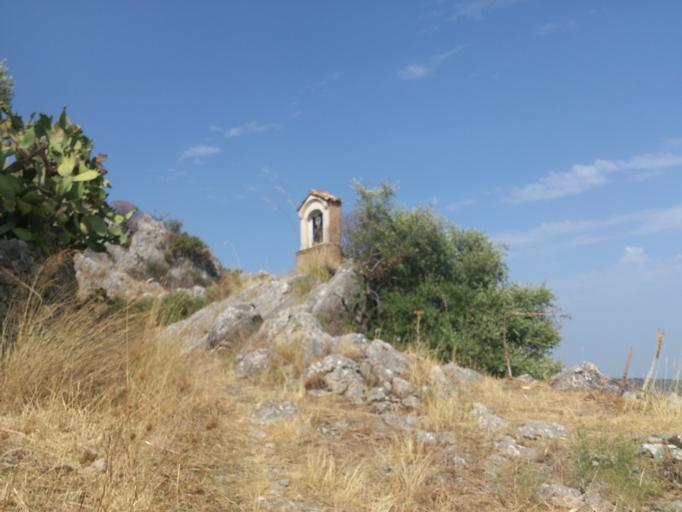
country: IT
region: Calabria
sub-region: Provincia di Reggio Calabria
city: Pazzano
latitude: 38.4688
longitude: 16.4552
